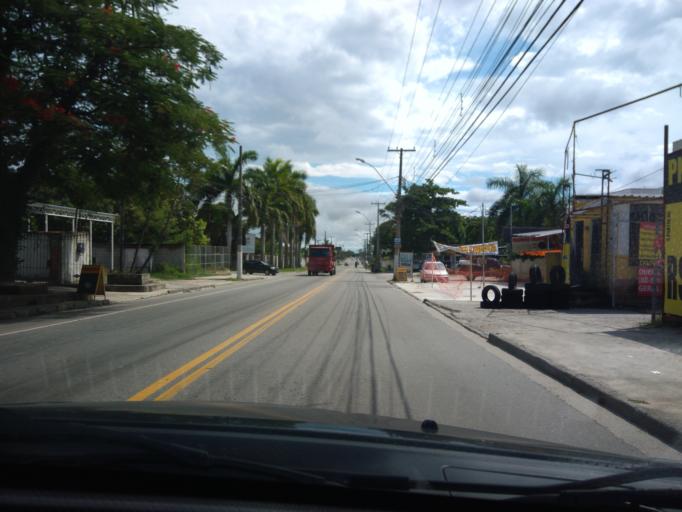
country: BR
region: Rio de Janeiro
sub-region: Niteroi
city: Niteroi
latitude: -22.9250
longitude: -43.0086
